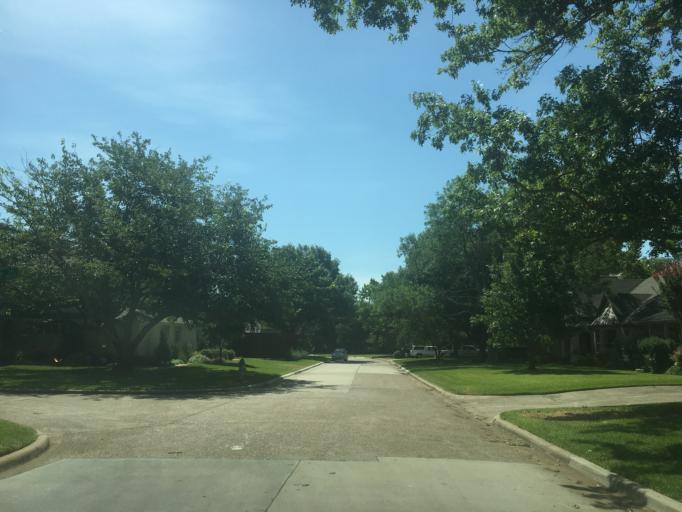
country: US
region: Texas
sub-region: Dallas County
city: Highland Park
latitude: 32.8660
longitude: -96.7211
